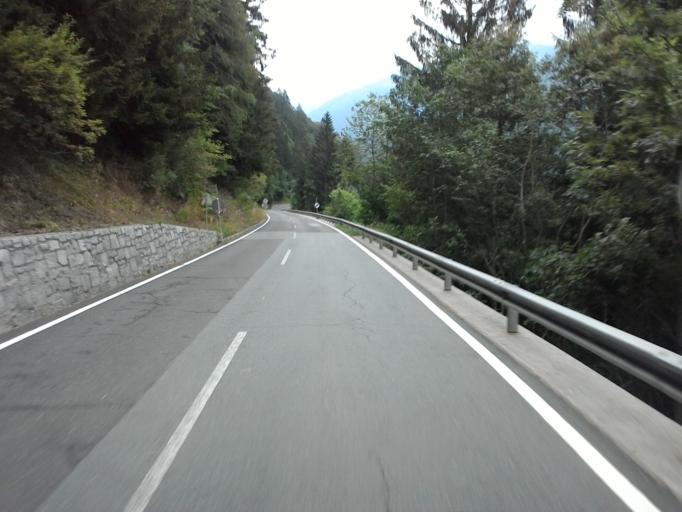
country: AT
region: Carinthia
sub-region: Politischer Bezirk Spittal an der Drau
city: Oberdrauburg
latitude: 46.6725
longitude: 12.9742
